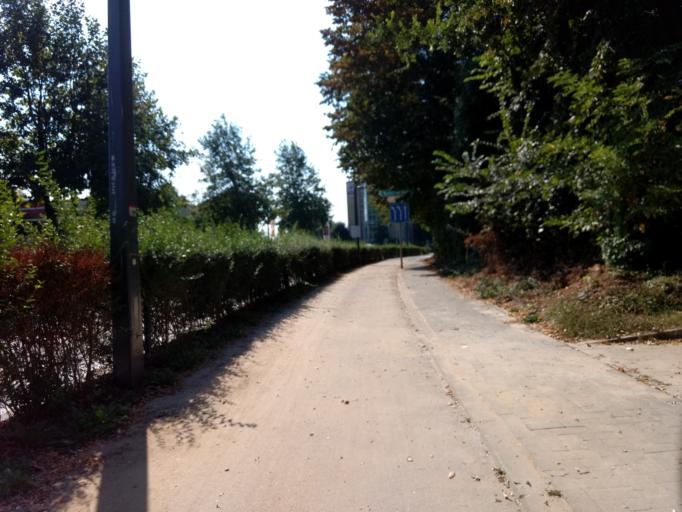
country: BE
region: Brussels Capital
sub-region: Bruxelles-Capitale
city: Brussels
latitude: 50.8195
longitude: 4.4032
